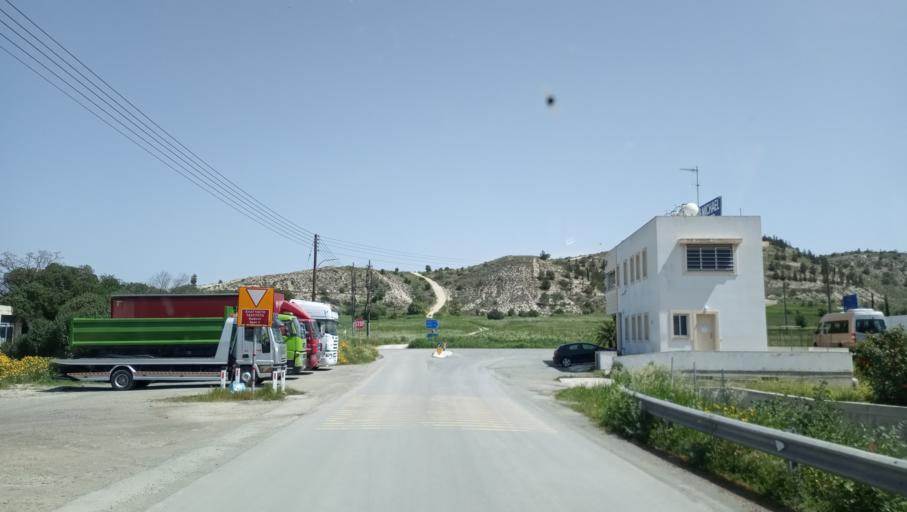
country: CY
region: Lefkosia
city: Alampra
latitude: 35.0071
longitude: 33.3932
